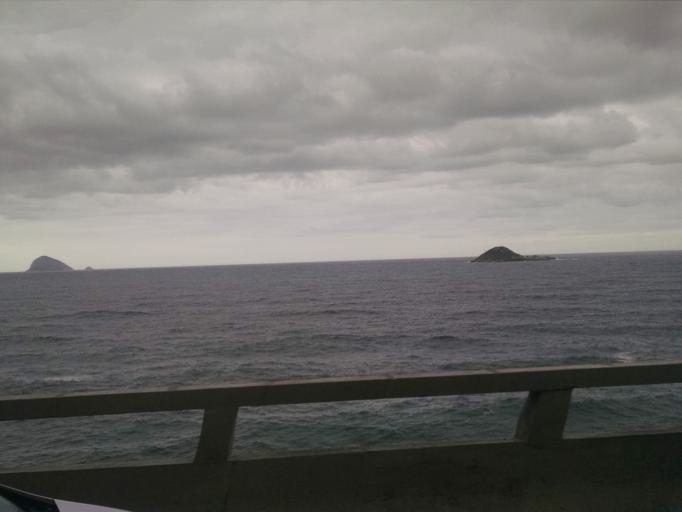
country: BR
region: Rio de Janeiro
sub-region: Rio De Janeiro
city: Rio de Janeiro
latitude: -23.0074
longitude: -43.2838
